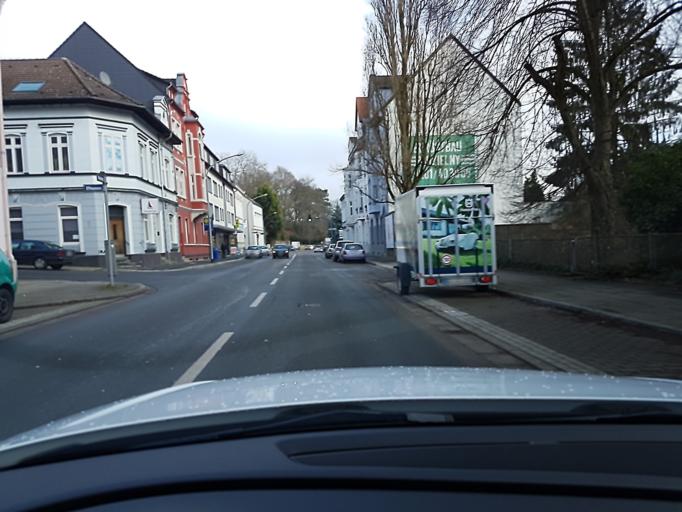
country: DE
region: North Rhine-Westphalia
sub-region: Regierungsbezirk Dusseldorf
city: Heiligenhaus
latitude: 51.3839
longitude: 6.9920
